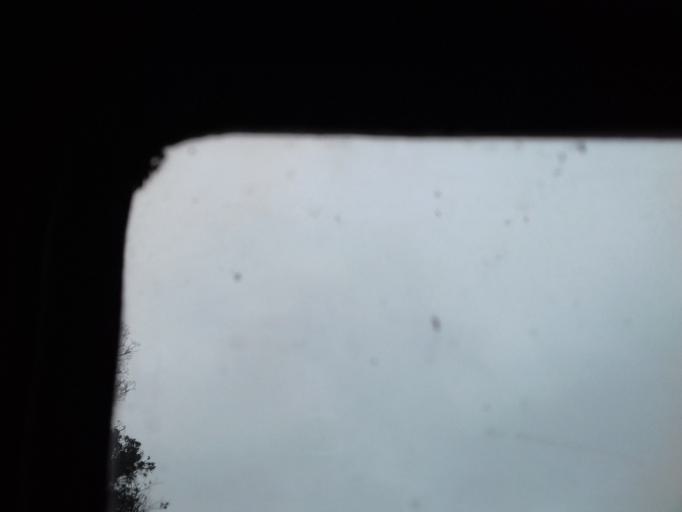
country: CO
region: Tolima
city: Murillo
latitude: 4.8862
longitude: -75.2515
